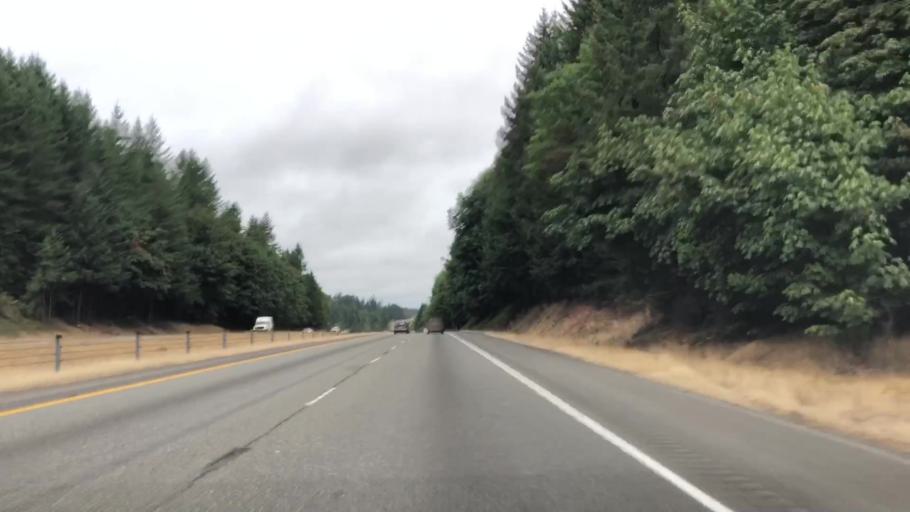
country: US
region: Washington
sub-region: Pierce County
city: Gig Harbor
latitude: 47.3248
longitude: -122.5935
